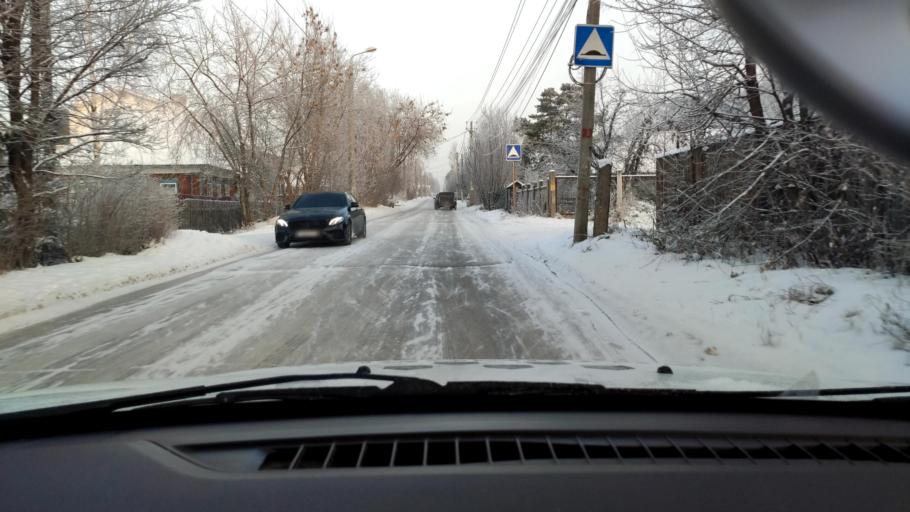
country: RU
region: Perm
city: Kondratovo
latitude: 58.0428
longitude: 56.1188
